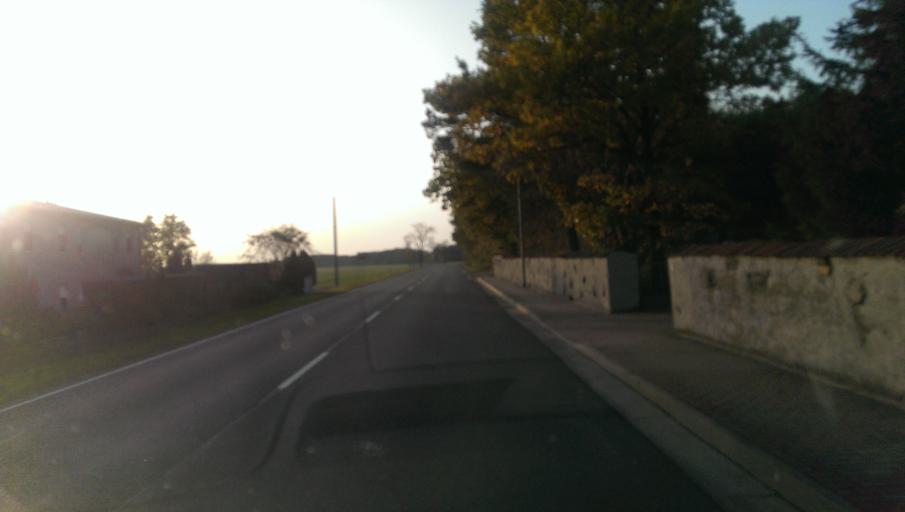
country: DE
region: Saxony-Anhalt
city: Holzdorf
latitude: 51.7795
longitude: 13.1087
